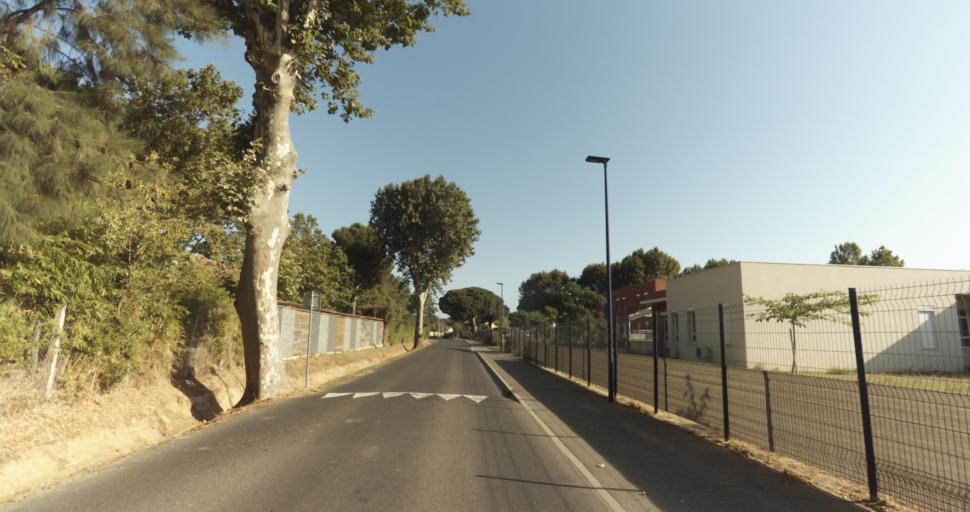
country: FR
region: Languedoc-Roussillon
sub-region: Departement des Pyrenees-Orientales
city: Alenya
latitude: 42.6373
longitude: 2.9861
